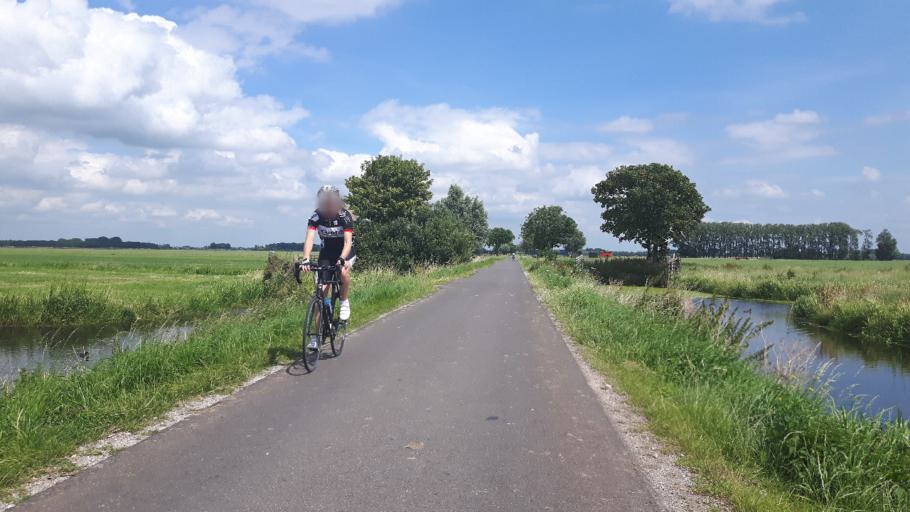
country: NL
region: South Holland
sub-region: Molenwaard
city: Nieuw-Lekkerland
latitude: 51.9158
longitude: 4.7211
